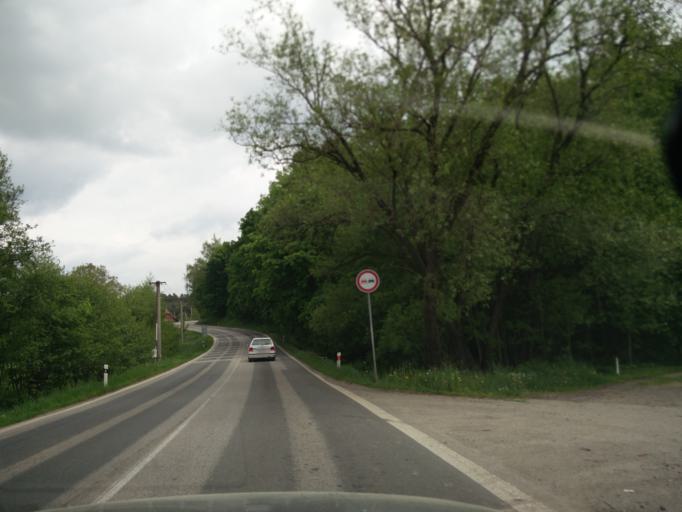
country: CZ
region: Jihocesky
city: Kamenny Ujezd
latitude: 48.8846
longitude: 14.4428
